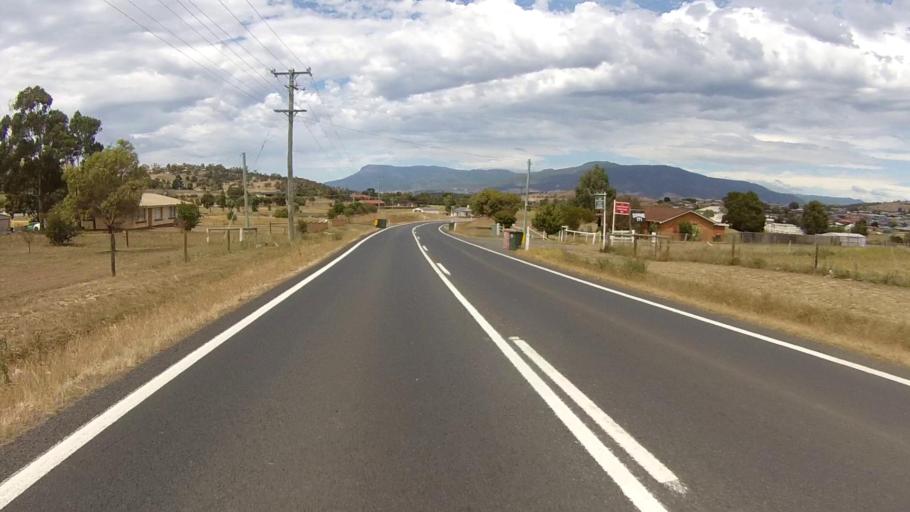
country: AU
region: Tasmania
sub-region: Brighton
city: Bridgewater
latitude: -42.6987
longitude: 147.2692
